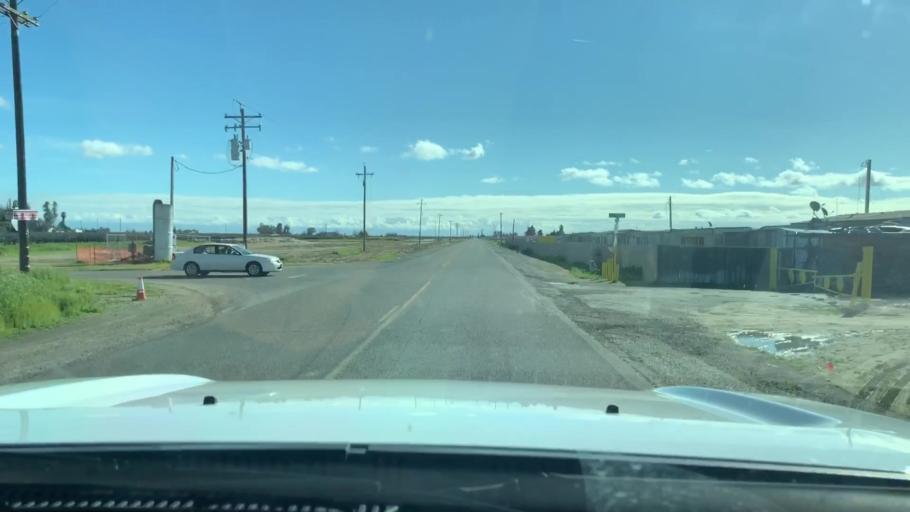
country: US
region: California
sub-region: Fresno County
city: Laton
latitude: 36.4893
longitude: -119.7013
